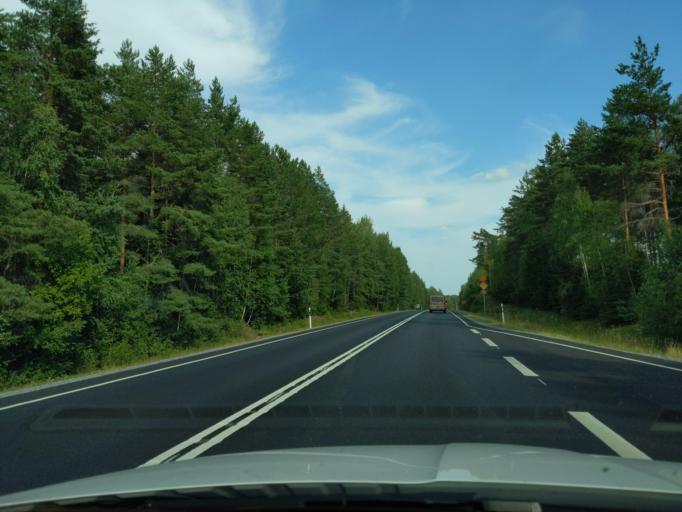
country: FI
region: Haeme
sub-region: Haemeenlinna
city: Hauho
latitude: 61.1723
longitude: 24.6120
